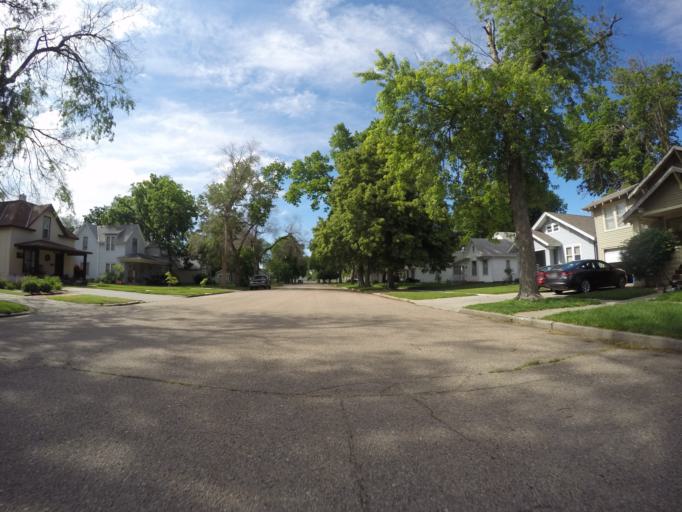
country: US
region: Nebraska
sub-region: Buffalo County
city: Kearney
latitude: 40.6965
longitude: -99.0900
